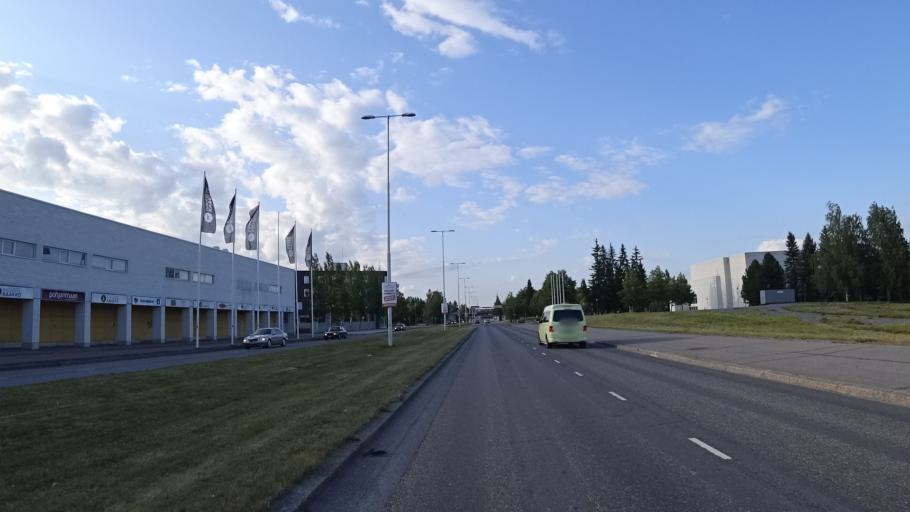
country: FI
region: South Karelia
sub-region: Imatra
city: Imatra
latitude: 61.1902
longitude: 28.7771
